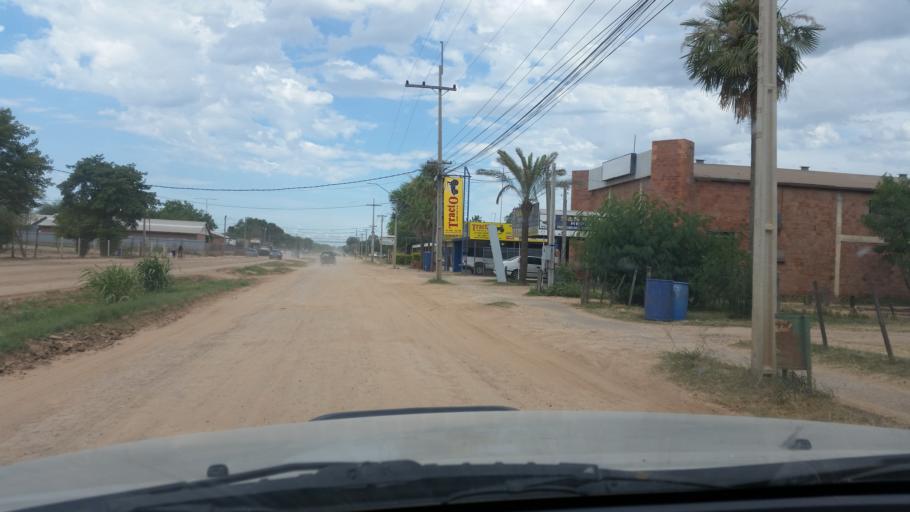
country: PY
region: Boqueron
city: Filadelfia
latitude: -22.3583
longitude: -60.0324
